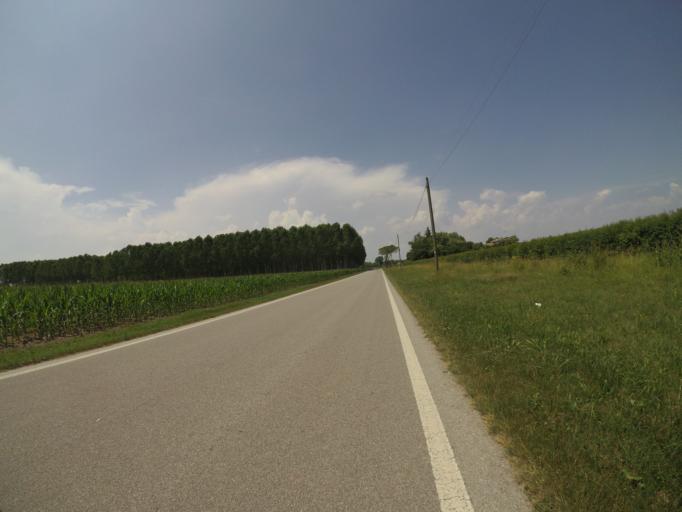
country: IT
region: Friuli Venezia Giulia
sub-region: Provincia di Udine
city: Rivignano
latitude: 45.8921
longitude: 13.0515
